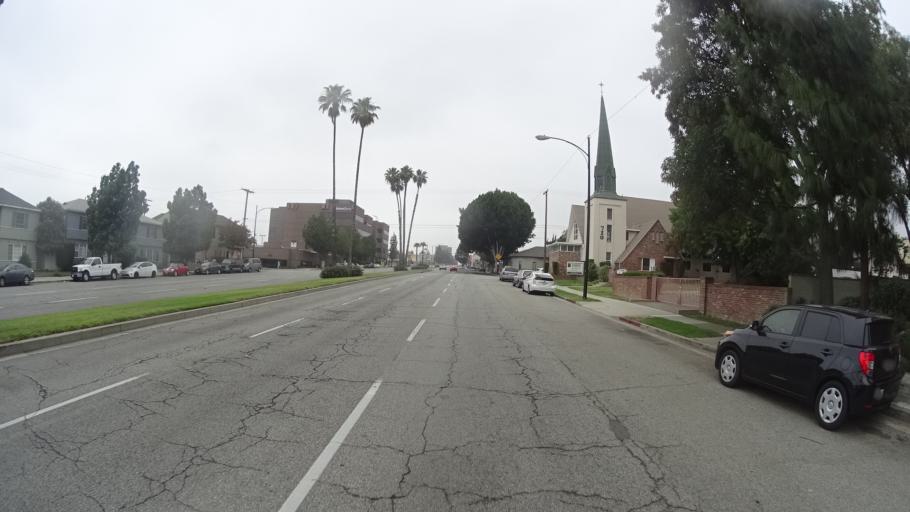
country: US
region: California
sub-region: Los Angeles County
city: Burbank
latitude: 34.1783
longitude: -118.2997
